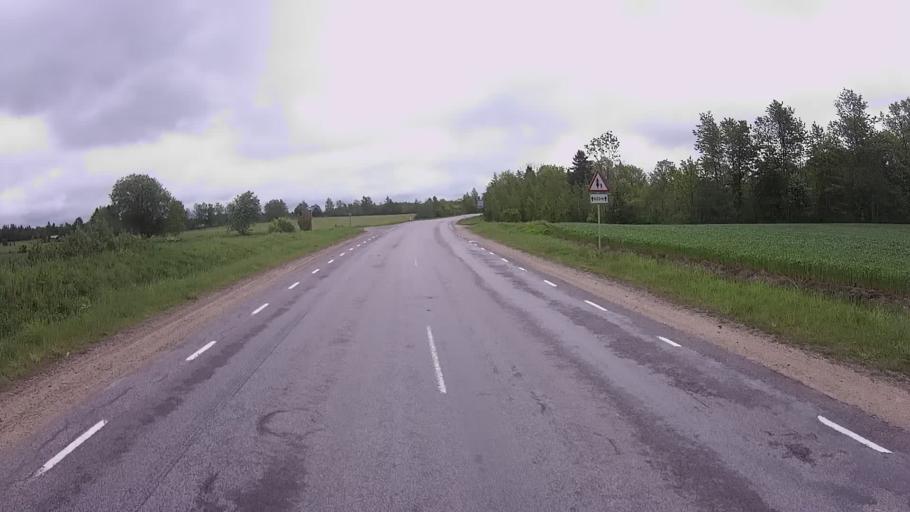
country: EE
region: Harju
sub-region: Nissi vald
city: Turba
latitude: 58.9166
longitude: 24.1894
